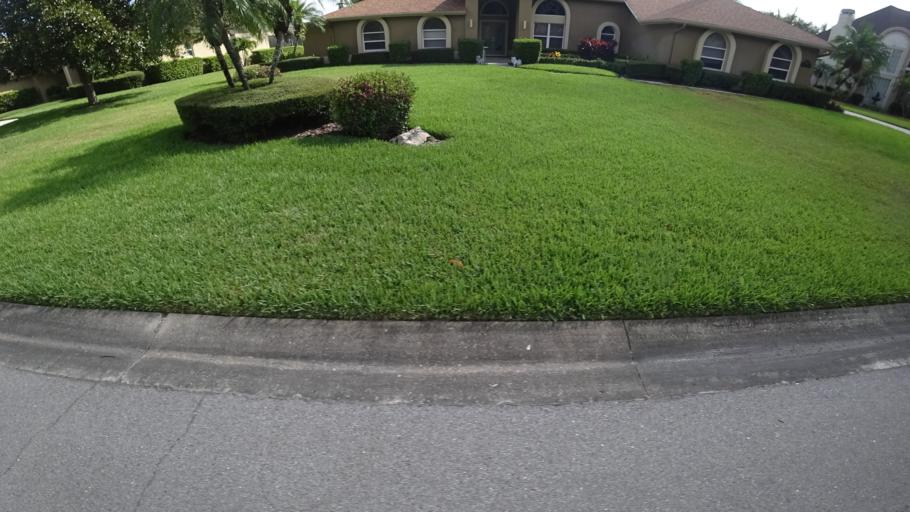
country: US
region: Florida
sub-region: Sarasota County
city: The Meadows
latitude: 27.4253
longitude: -82.4381
